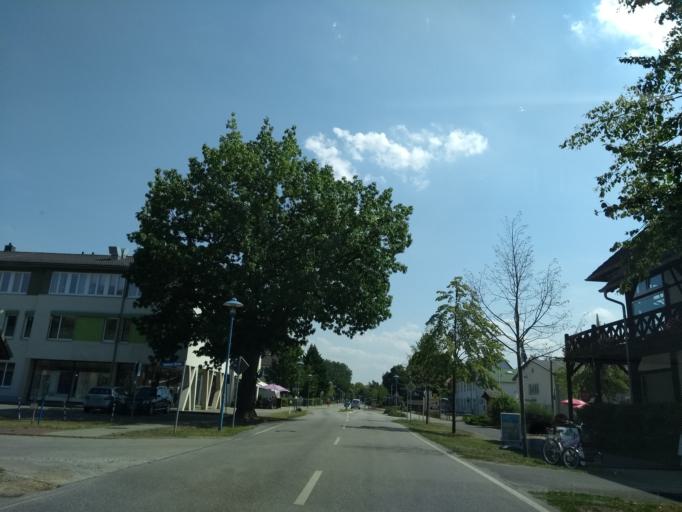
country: DE
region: Brandenburg
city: Burg
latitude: 51.8371
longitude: 14.1409
